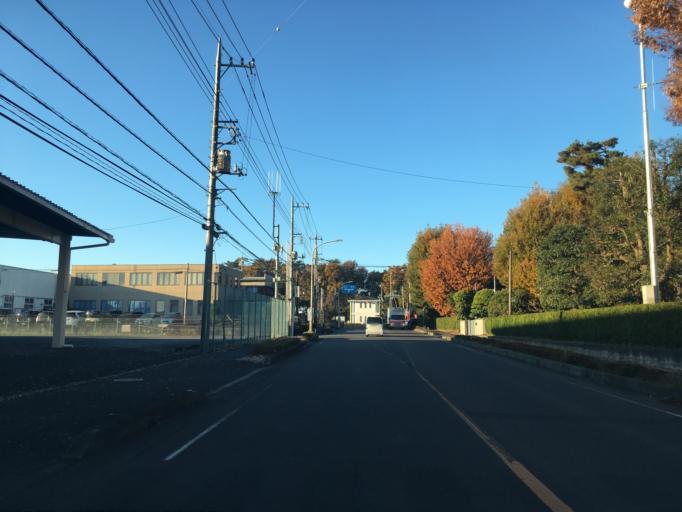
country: JP
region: Saitama
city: Sayama
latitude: 35.8183
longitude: 139.3913
